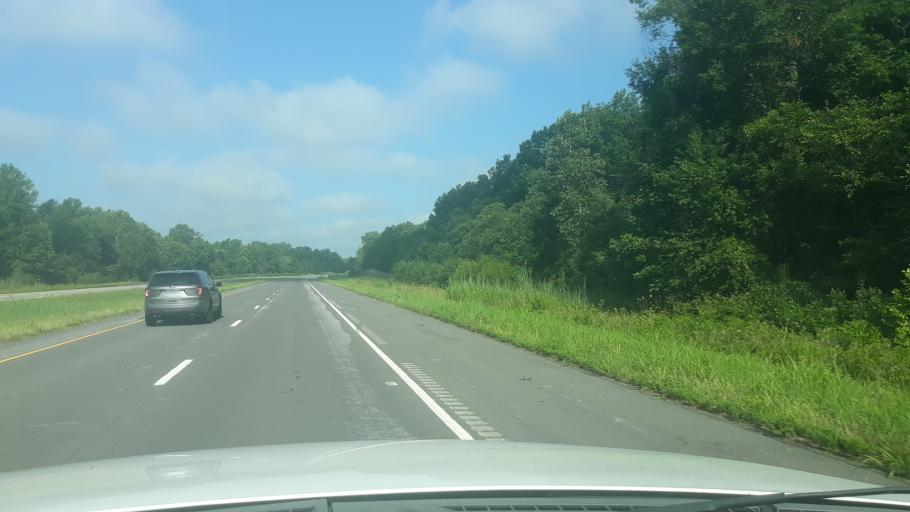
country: US
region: Illinois
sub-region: Saline County
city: Carrier Mills
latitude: 37.7345
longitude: -88.6932
